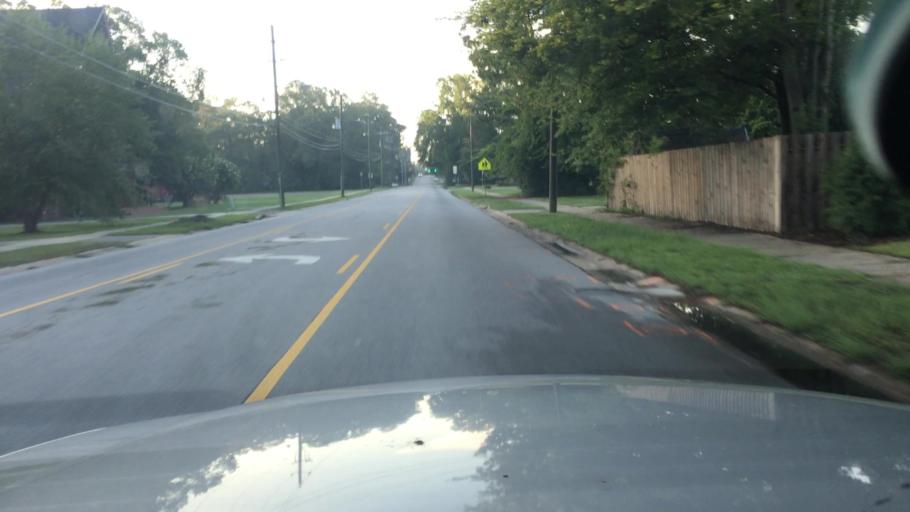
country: US
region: North Carolina
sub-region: Cumberland County
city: Fayetteville
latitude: 35.0683
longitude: -78.9195
